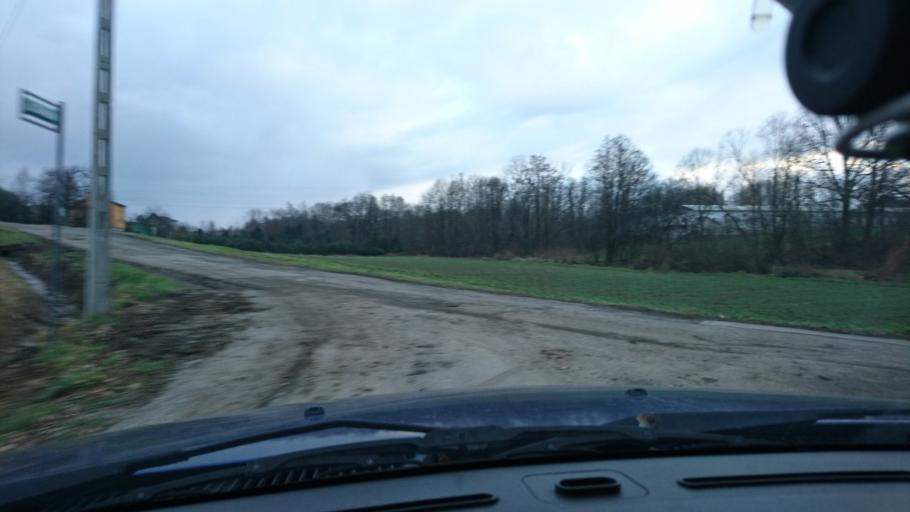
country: PL
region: Silesian Voivodeship
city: Janowice
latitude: 49.8945
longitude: 19.0811
